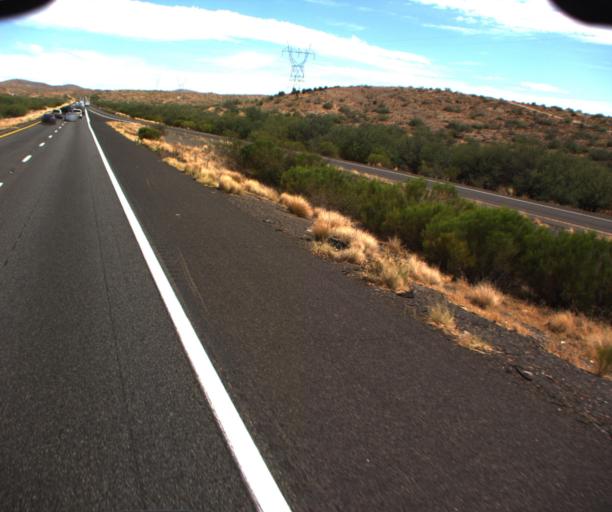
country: US
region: Arizona
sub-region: Yavapai County
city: Cordes Lakes
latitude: 34.2387
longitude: -112.1117
